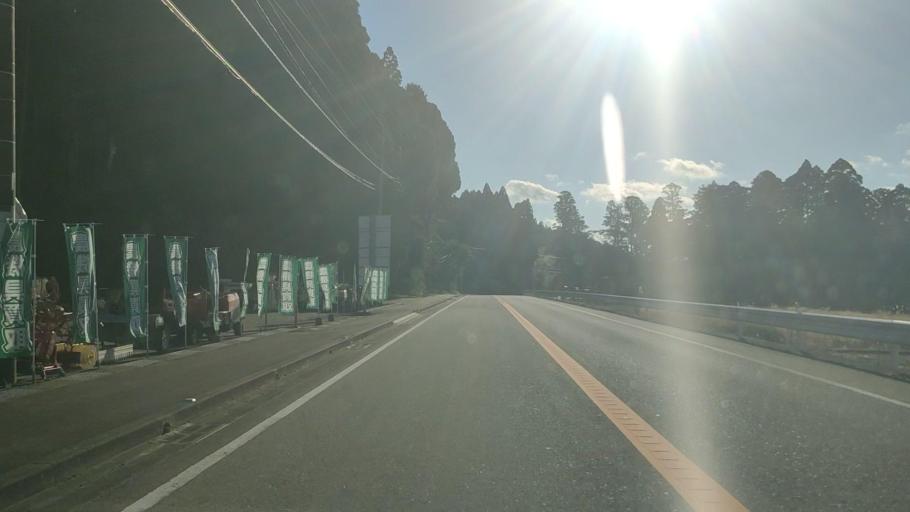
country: JP
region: Fukuoka
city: Maebaru-chuo
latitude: 33.4462
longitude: 130.2716
